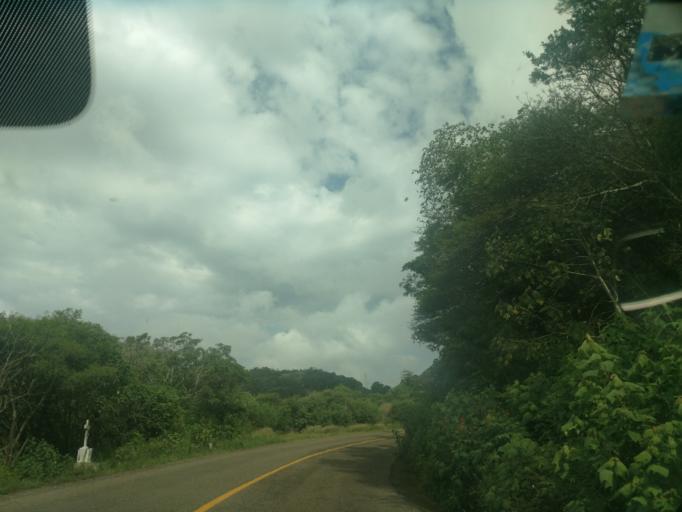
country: MX
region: Jalisco
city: El Salto
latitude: 20.3625
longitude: -104.5888
